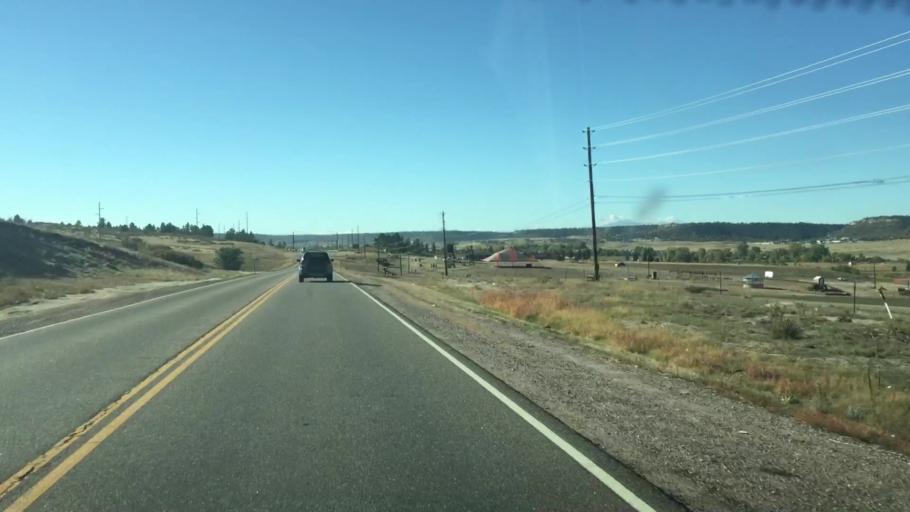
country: US
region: Colorado
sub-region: Douglas County
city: The Pinery
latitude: 39.4218
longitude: -104.7609
